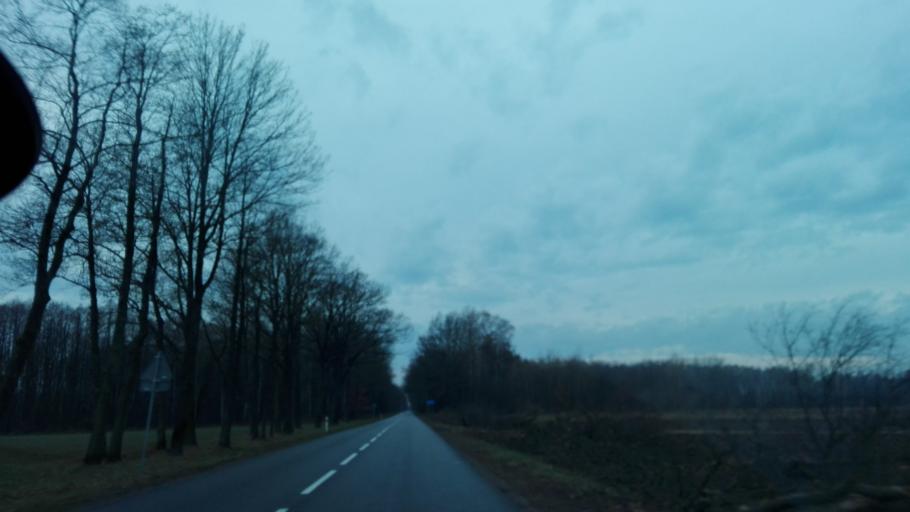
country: PL
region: Lublin Voivodeship
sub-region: Powiat radzynski
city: Wohyn
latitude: 51.7824
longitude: 22.7365
